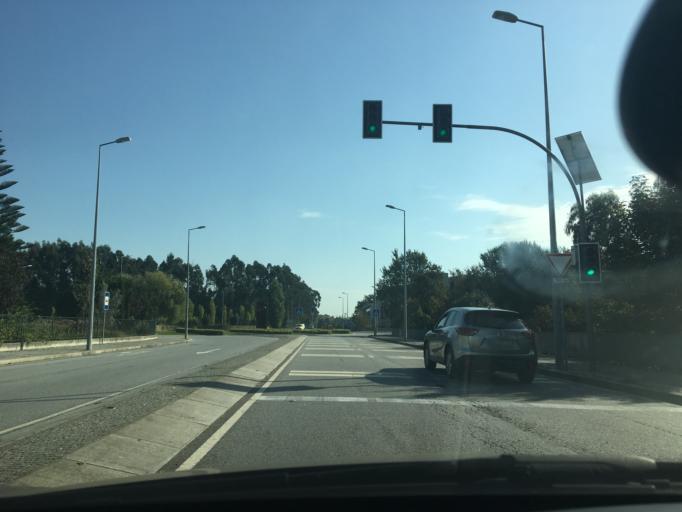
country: PT
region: Porto
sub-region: Maia
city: Maia
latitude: 41.2354
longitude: -8.6405
